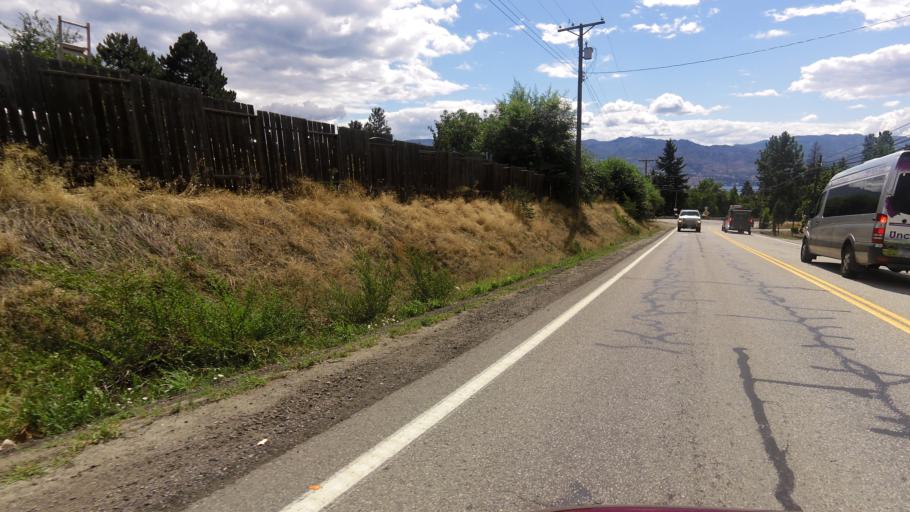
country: CA
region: British Columbia
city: West Kelowna
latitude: 49.8501
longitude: -119.5565
